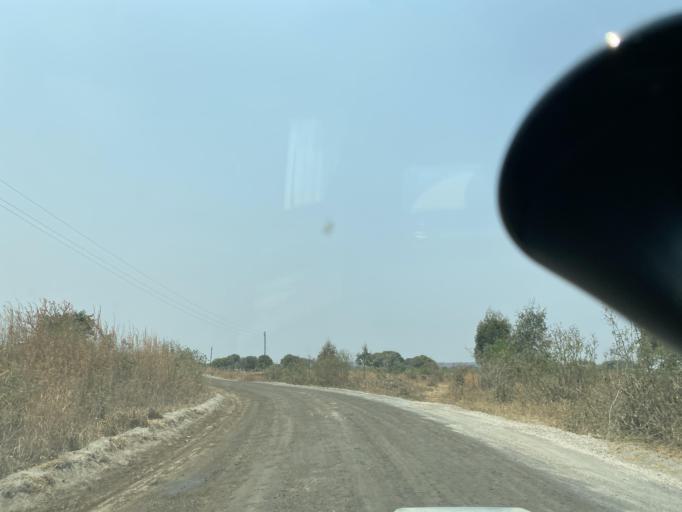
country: ZM
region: Lusaka
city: Lusaka
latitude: -15.5607
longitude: 28.4345
